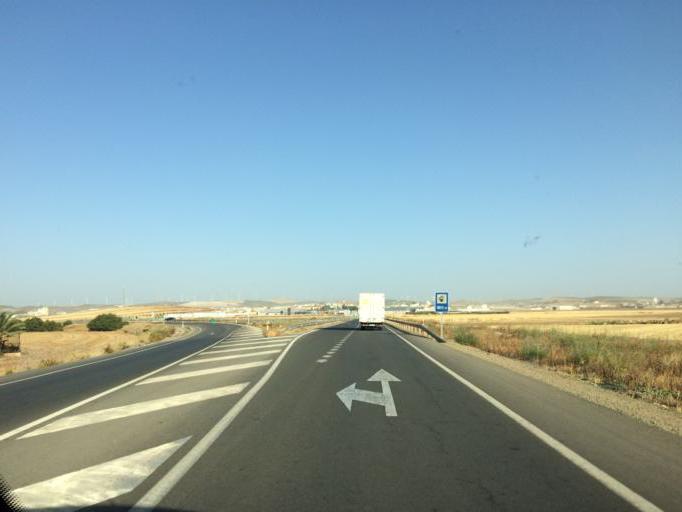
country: ES
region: Andalusia
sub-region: Provincia de Malaga
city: Campillos
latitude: 37.0489
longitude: -4.8425
